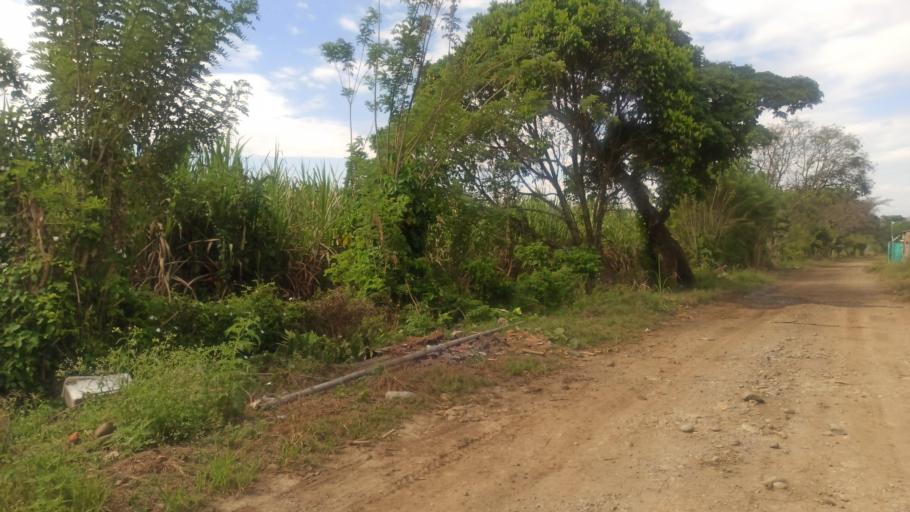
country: CO
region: Valle del Cauca
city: Jamundi
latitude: 3.1708
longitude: -76.5922
